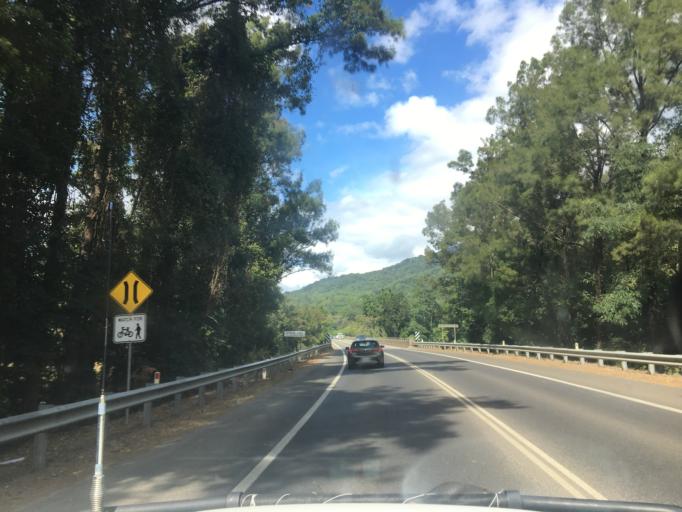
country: AU
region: Queensland
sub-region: Cairns
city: Redlynch
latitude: -16.8713
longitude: 145.6860
